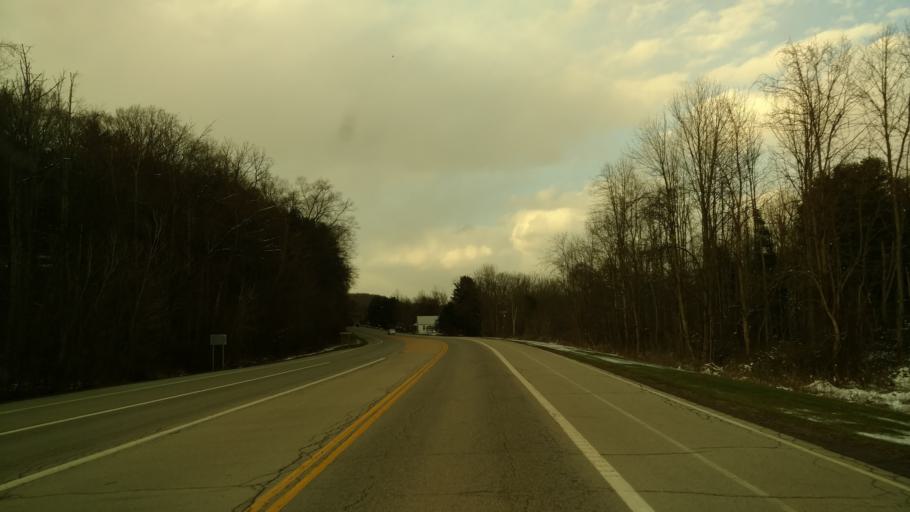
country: US
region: Ohio
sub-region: Ashland County
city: Loudonville
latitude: 40.6099
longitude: -82.2571
